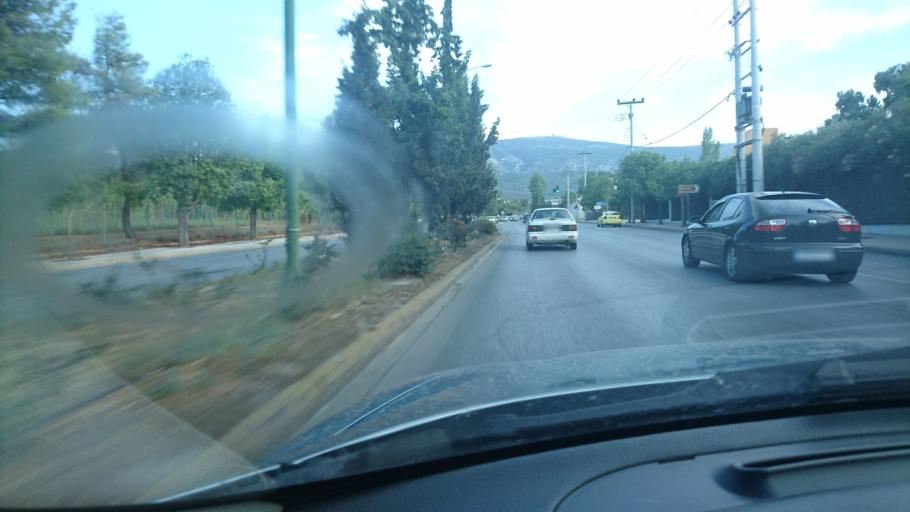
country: GR
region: Attica
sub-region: Nomarchia Athinas
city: Papagou
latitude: 37.9873
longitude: 23.7802
